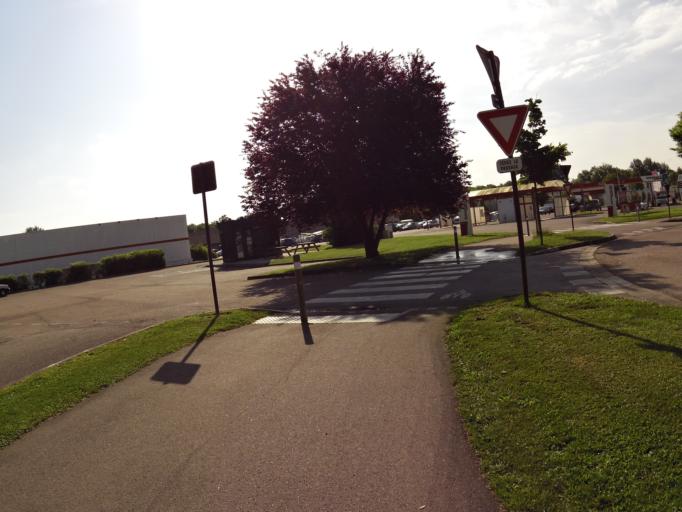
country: FR
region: Champagne-Ardenne
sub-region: Departement de l'Aube
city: Saint-Julien-les-Villas
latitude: 48.2816
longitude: 4.0943
